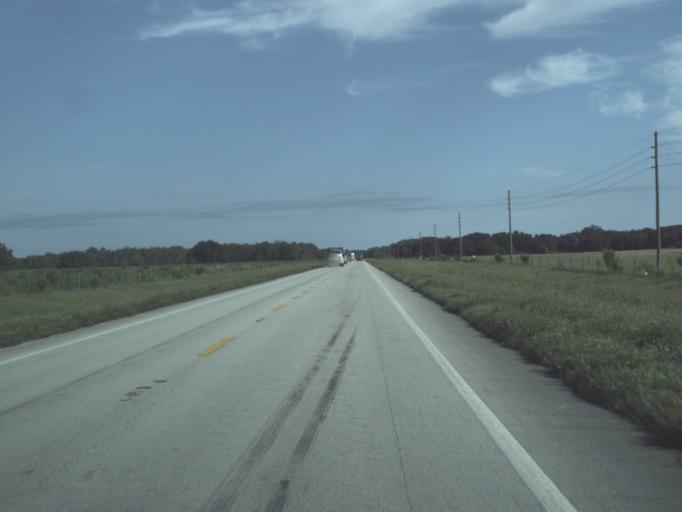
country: US
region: Florida
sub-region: Okeechobee County
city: Cypress Quarters
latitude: 27.4799
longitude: -80.8072
